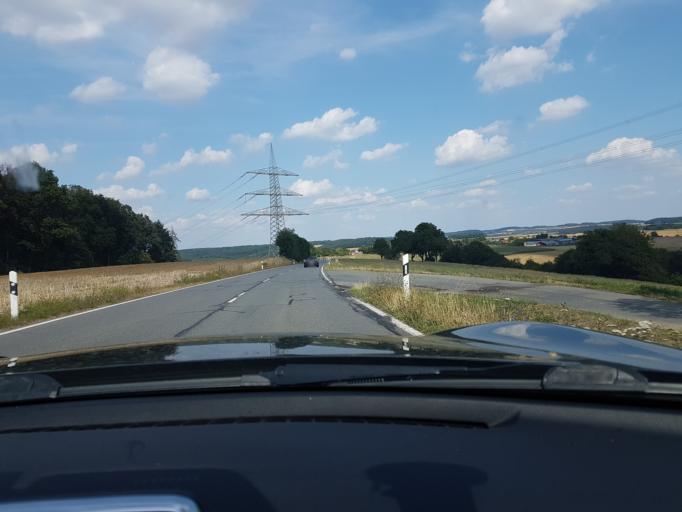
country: DE
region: Baden-Wuerttemberg
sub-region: Karlsruhe Region
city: Mosbach
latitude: 49.3461
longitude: 9.1999
